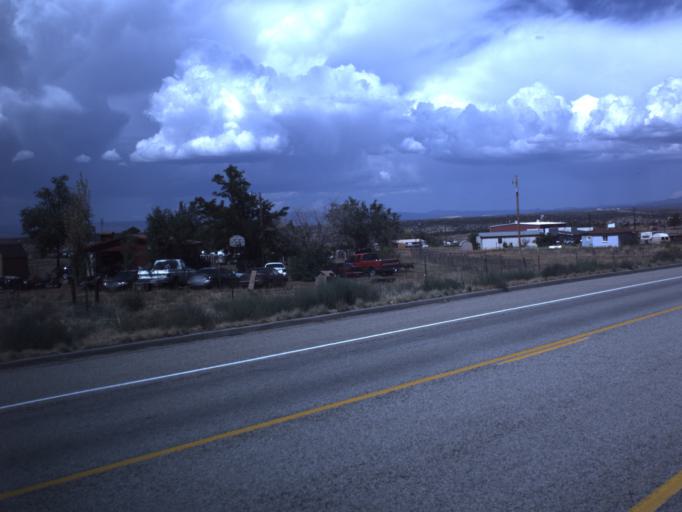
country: US
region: Utah
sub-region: San Juan County
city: Blanding
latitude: 37.4608
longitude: -109.4670
